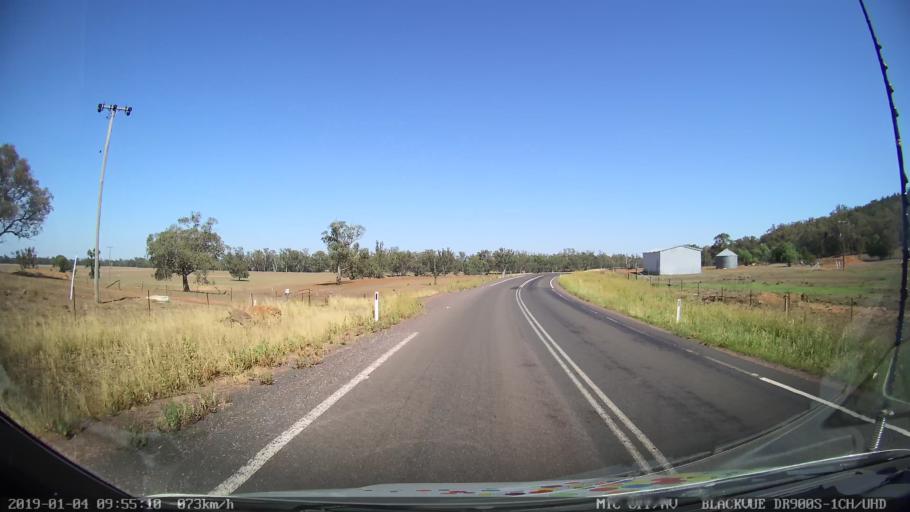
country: AU
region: New South Wales
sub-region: Cabonne
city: Canowindra
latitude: -33.5361
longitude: 148.4066
